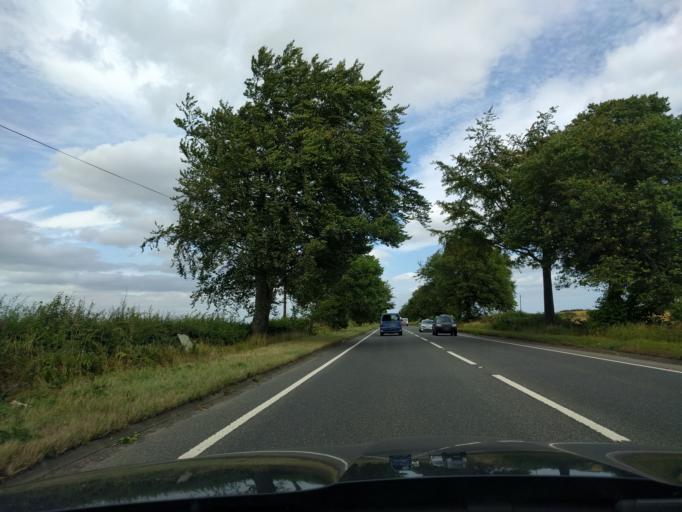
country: GB
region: England
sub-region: Northumberland
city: Hebron
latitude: 55.2044
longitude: -1.7115
